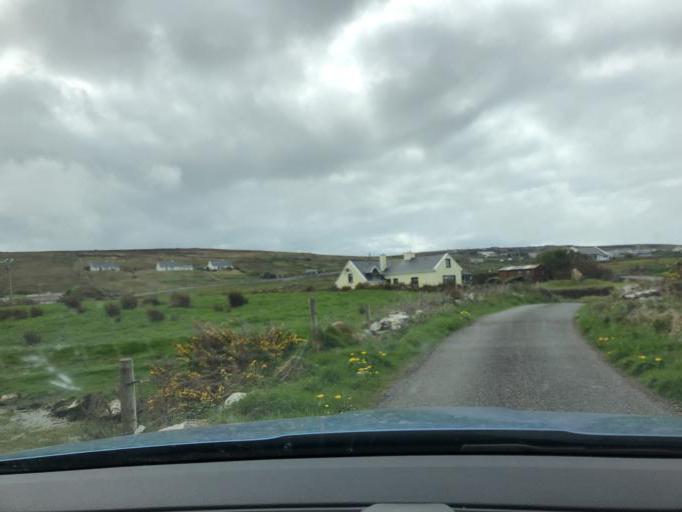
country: IE
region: Munster
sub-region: An Clar
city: Kilrush
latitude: 52.9932
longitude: -9.4049
